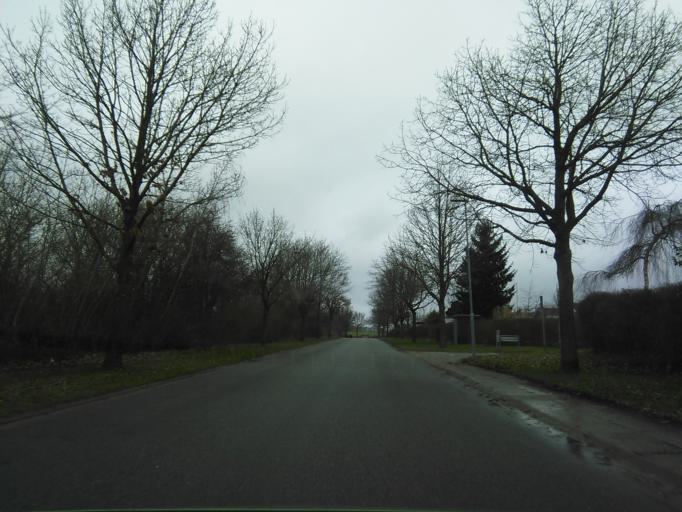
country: DK
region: Central Jutland
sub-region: Arhus Kommune
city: Tranbjerg
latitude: 56.0917
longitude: 10.1434
